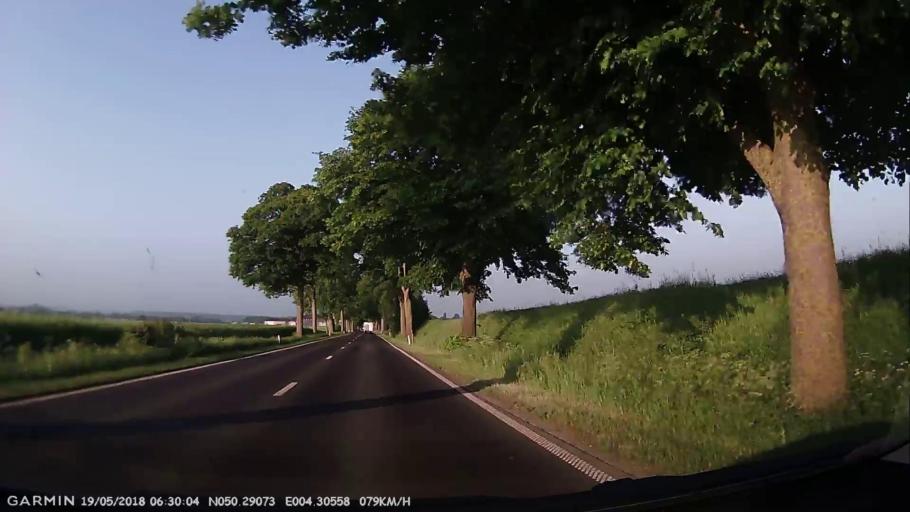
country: BE
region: Wallonia
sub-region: Province du Hainaut
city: Thuin
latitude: 50.2907
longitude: 4.3056
